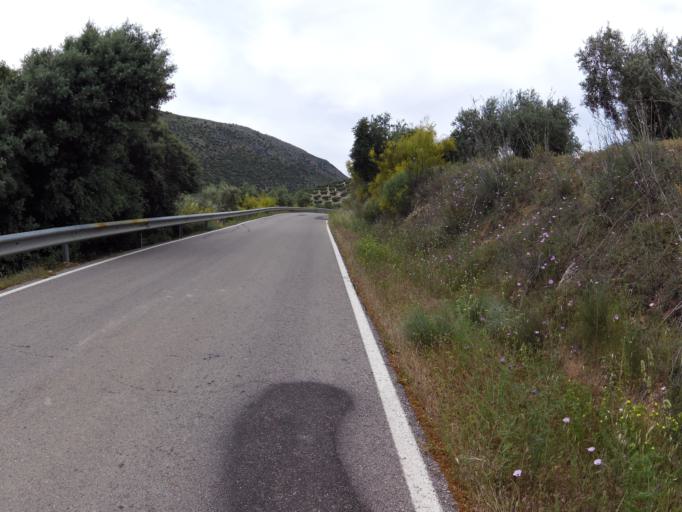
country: ES
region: Andalusia
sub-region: Province of Cordoba
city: Fuente-Tojar
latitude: 37.5183
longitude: -4.2155
